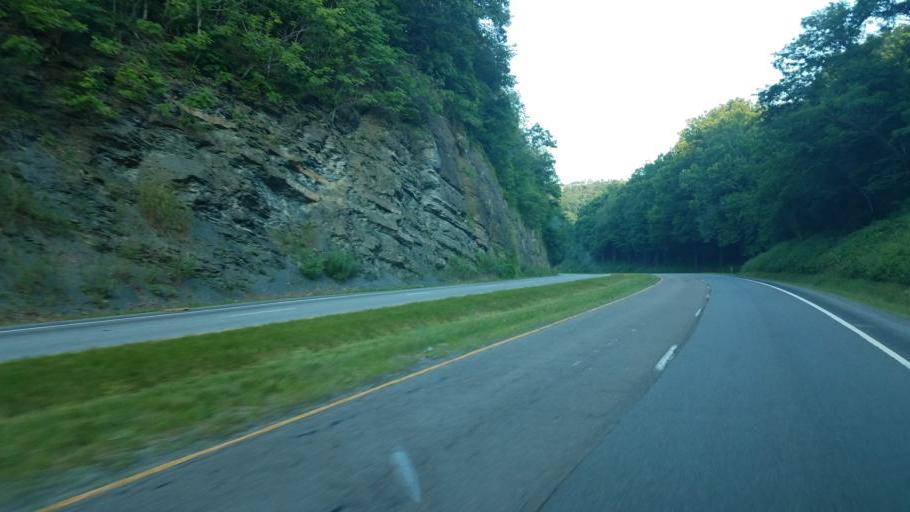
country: US
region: Virginia
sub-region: Wise County
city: Big Stone Gap
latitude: 36.7018
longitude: -82.7743
